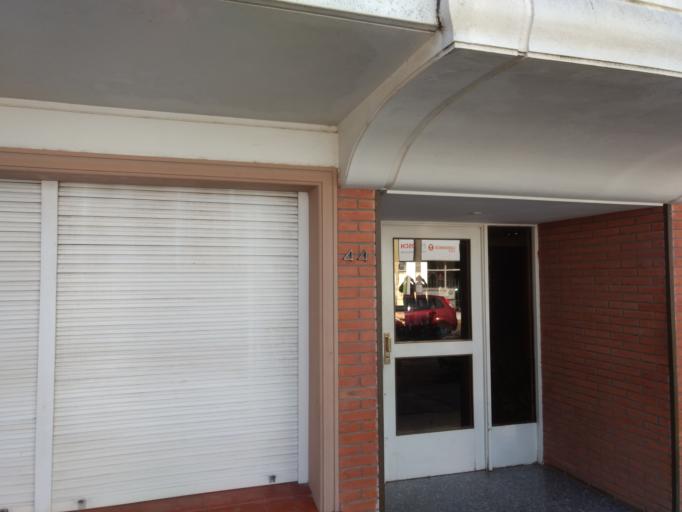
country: AR
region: Buenos Aires
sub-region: Partido de Lobos
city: Lobos
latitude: -35.1775
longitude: -59.0970
